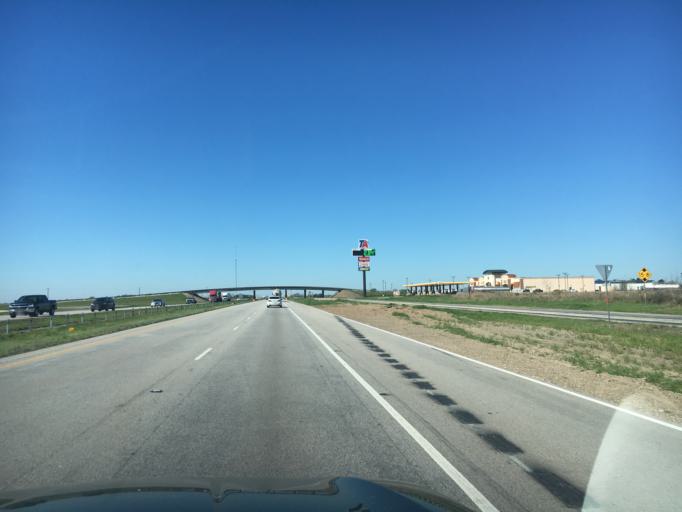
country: US
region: Texas
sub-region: Colorado County
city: Eagle Lake
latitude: 29.7423
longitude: -96.3270
